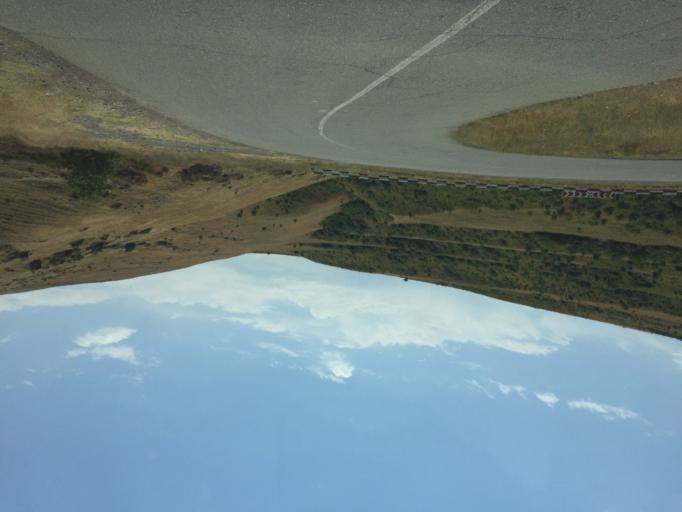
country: AZ
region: Lacin
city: Lacin
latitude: 39.5829
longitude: 46.5276
